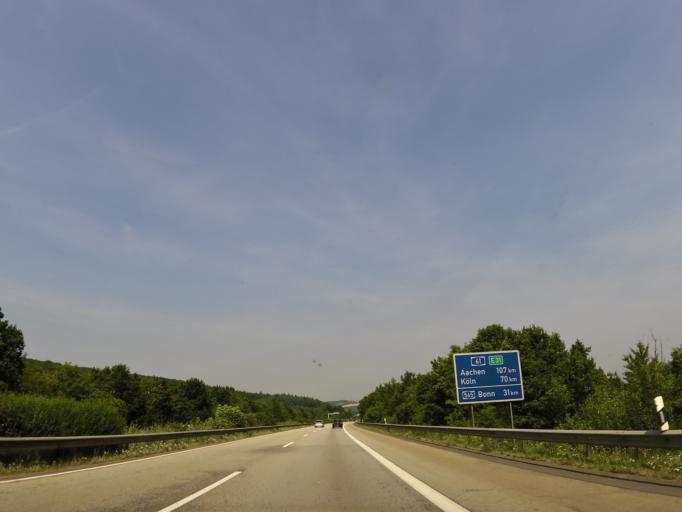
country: DE
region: Rheinland-Pfalz
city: Konigsfeld
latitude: 50.5333
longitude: 7.1766
